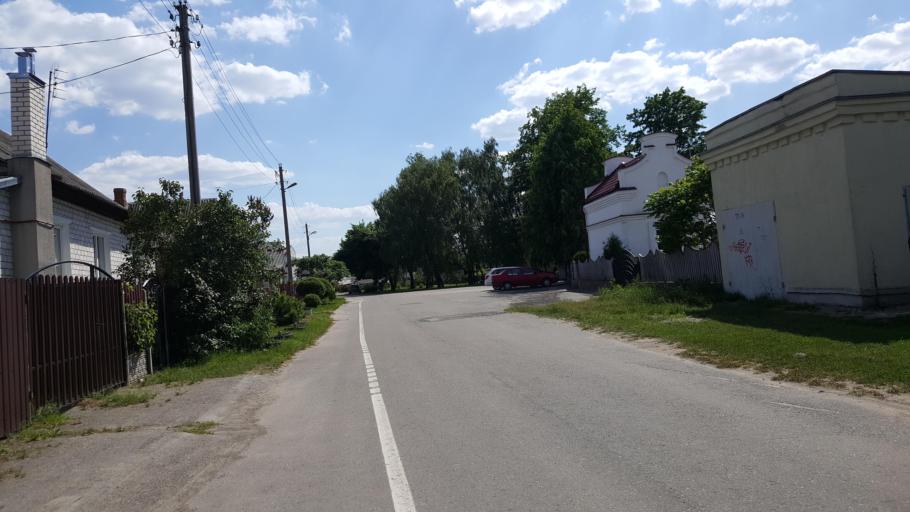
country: BY
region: Brest
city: Kobryn
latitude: 52.2152
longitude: 24.3569
